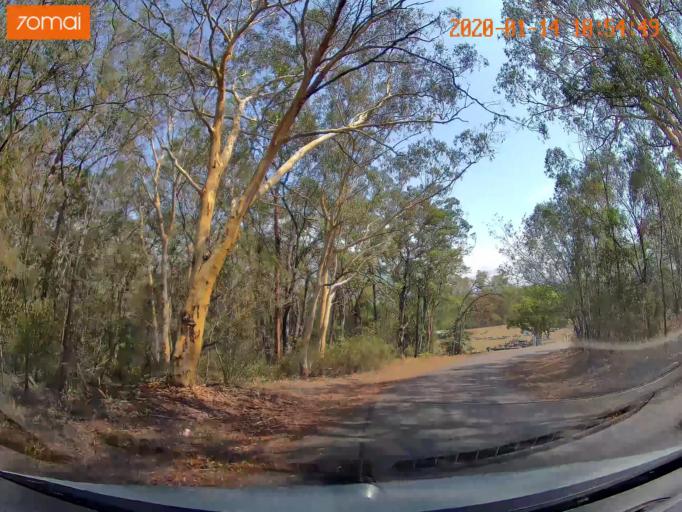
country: AU
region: New South Wales
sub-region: Lake Macquarie Shire
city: Dora Creek
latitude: -33.0970
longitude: 151.4858
